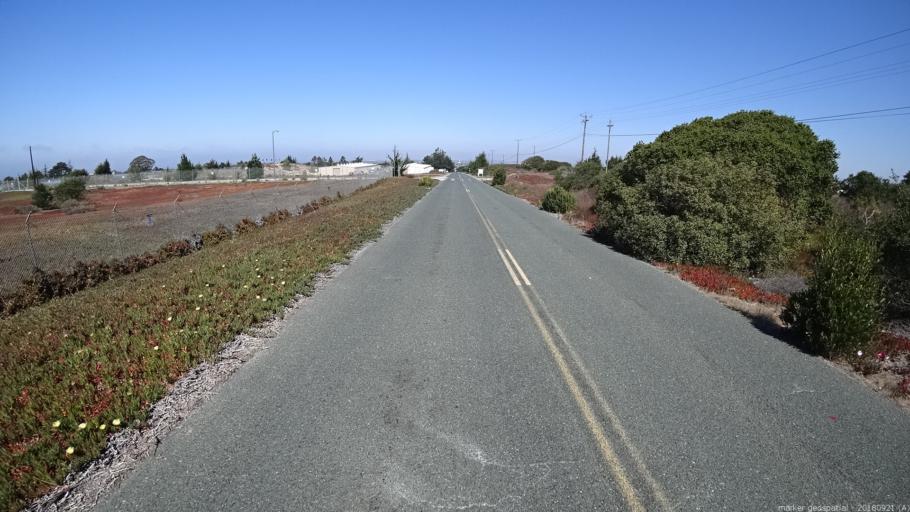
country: US
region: California
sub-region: Monterey County
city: Marina
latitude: 36.6456
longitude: -121.7872
